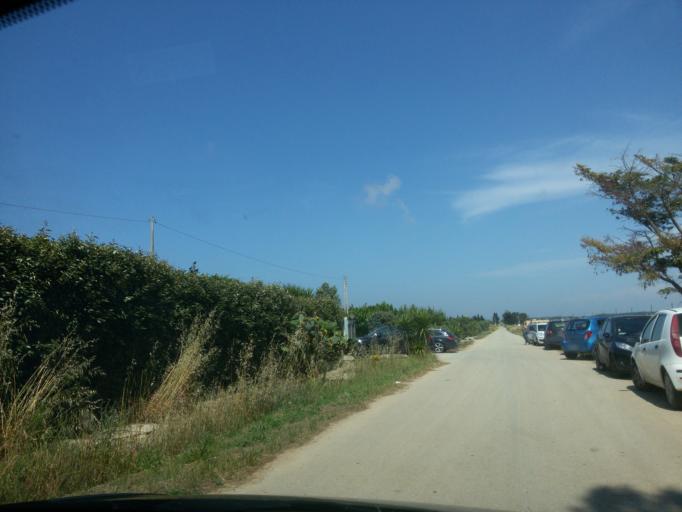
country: IT
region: Apulia
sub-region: Provincia di Brindisi
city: Brindisi
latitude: 40.6599
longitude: 17.8516
